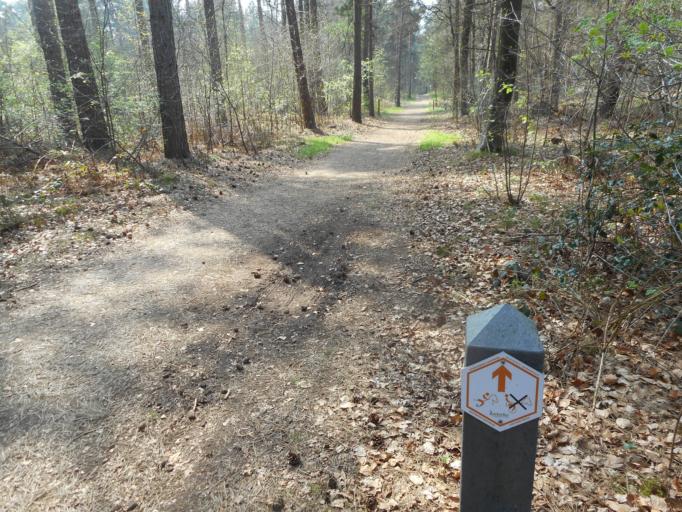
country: BE
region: Flanders
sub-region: Provincie Antwerpen
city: Kasterlee
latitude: 51.2330
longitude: 4.9446
